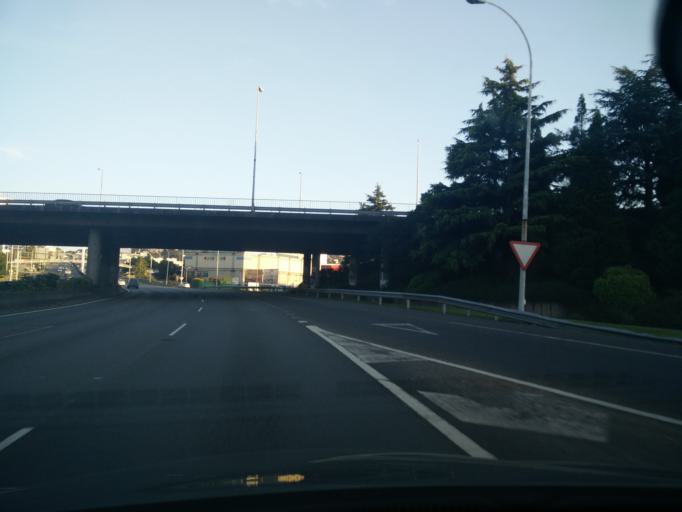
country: ES
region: Galicia
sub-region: Provincia da Coruna
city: A Coruna
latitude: 43.3434
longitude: -8.4090
